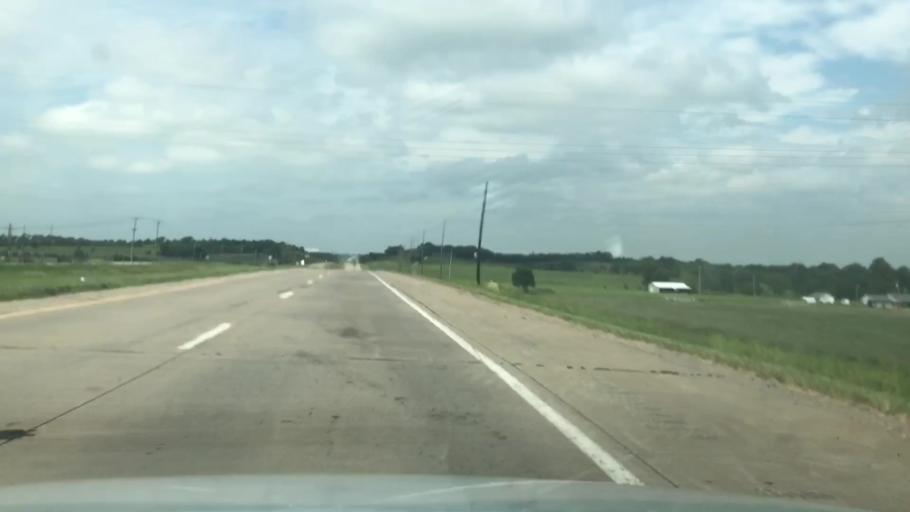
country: US
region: Oklahoma
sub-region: Osage County
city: Skiatook
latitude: 36.5378
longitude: -95.9276
